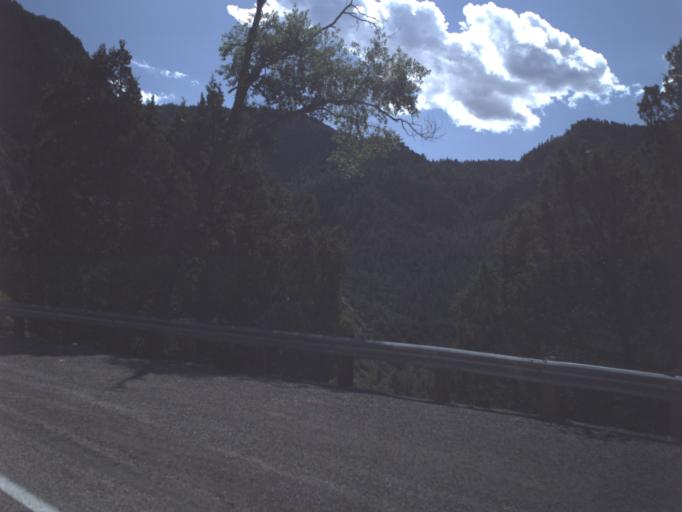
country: US
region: Utah
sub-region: Beaver County
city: Beaver
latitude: 38.2711
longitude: -112.4811
